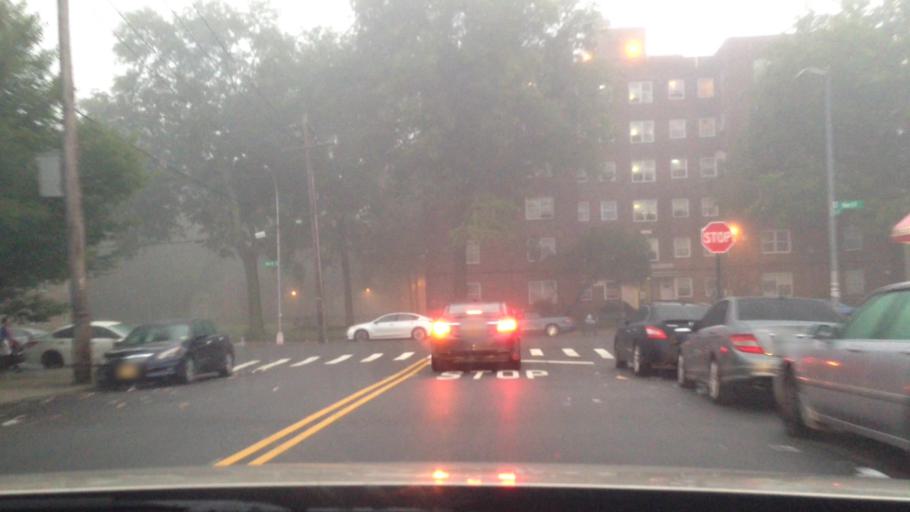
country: US
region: New York
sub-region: Kings County
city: Brooklyn
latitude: 40.5992
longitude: -73.9369
